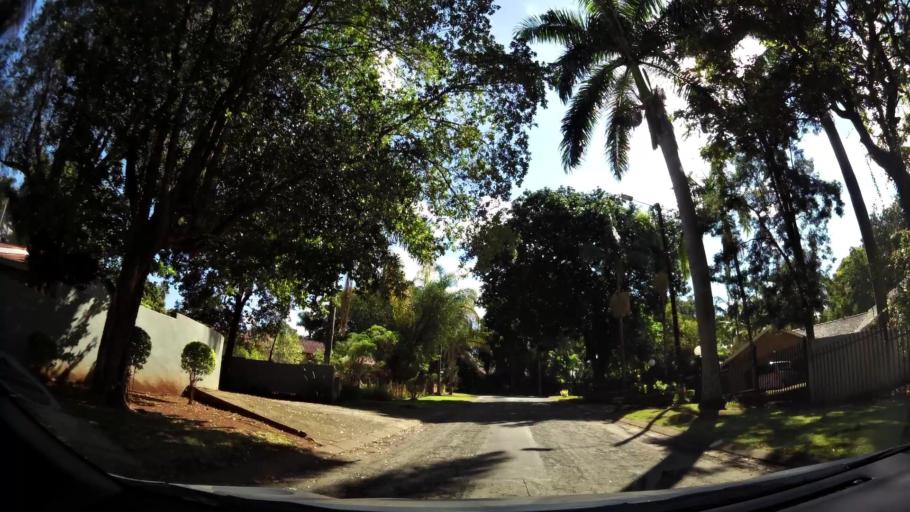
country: ZA
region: Limpopo
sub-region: Mopani District Municipality
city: Tzaneen
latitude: -23.8181
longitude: 30.1484
